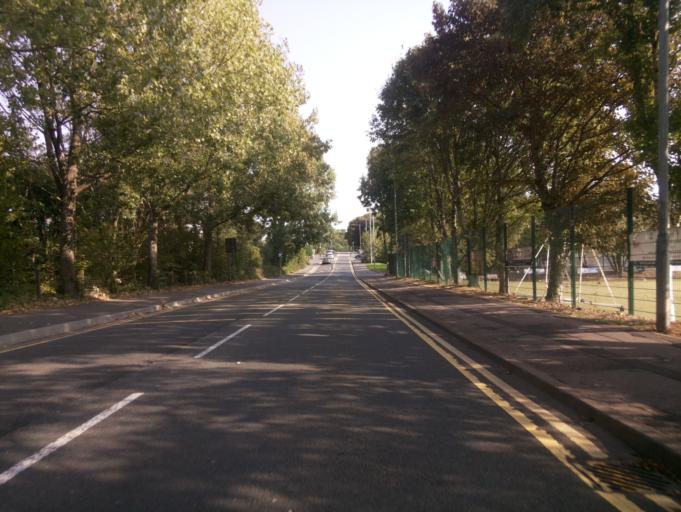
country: GB
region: Wales
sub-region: Newport
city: Newport
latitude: 51.6066
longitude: -3.0120
